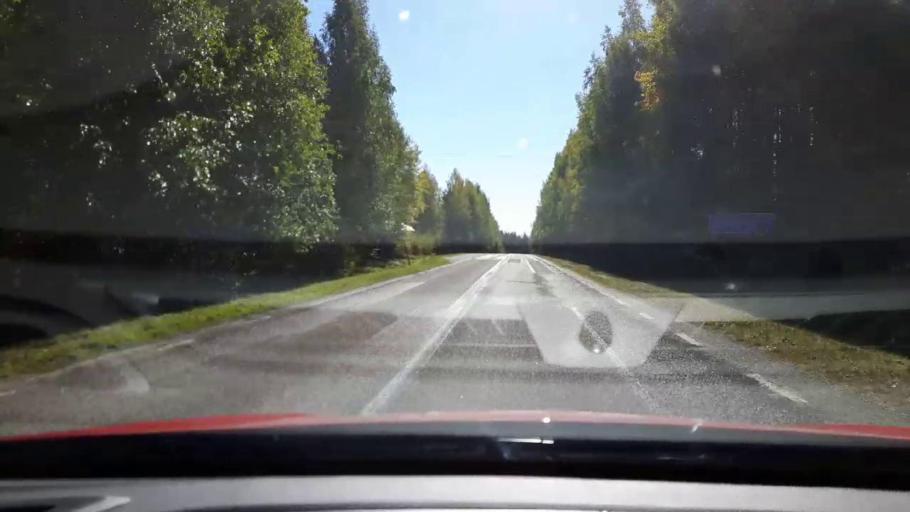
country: SE
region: Jaemtland
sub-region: Harjedalens Kommun
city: Sveg
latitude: 62.1252
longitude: 14.1638
